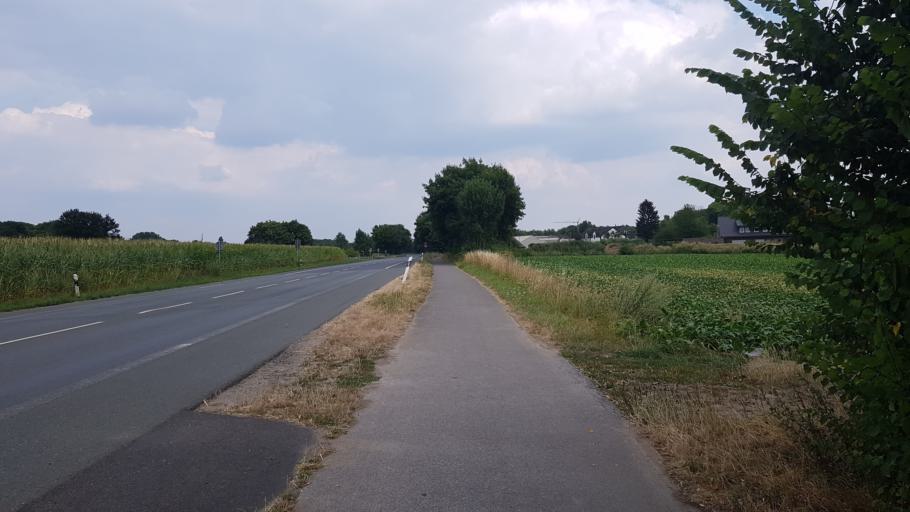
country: DE
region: North Rhine-Westphalia
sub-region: Regierungsbezirk Dusseldorf
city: Kamp-Lintfort
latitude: 51.4643
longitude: 6.5675
